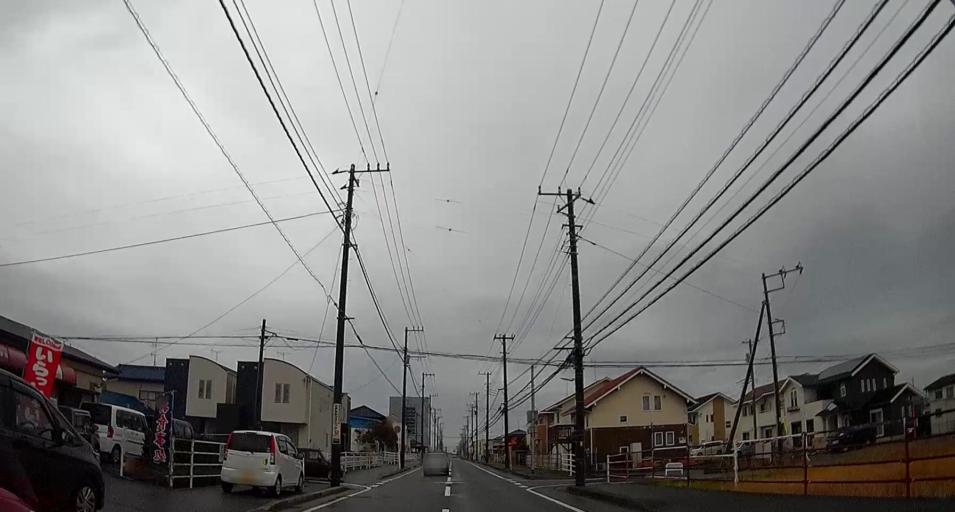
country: JP
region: Chiba
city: Kisarazu
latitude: 35.4357
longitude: 139.9619
